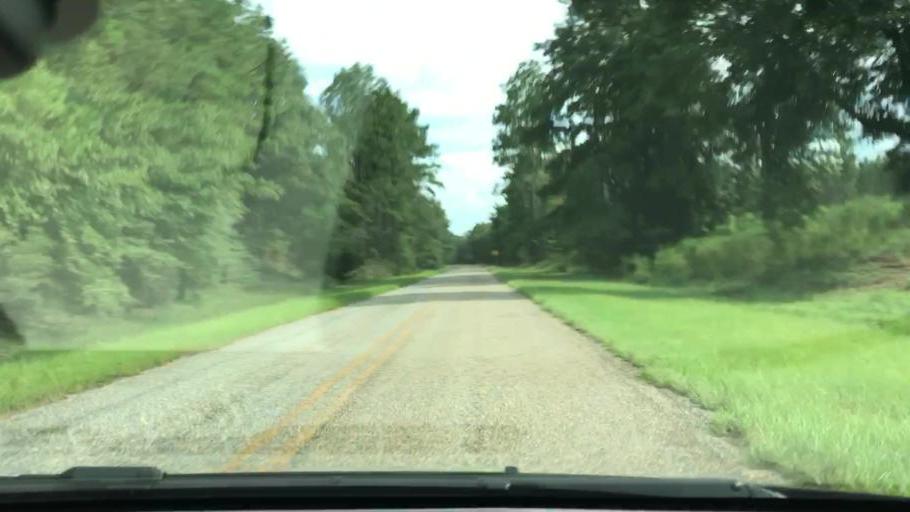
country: US
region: Georgia
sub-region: Clay County
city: Fort Gaines
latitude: 31.5128
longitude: -84.9529
